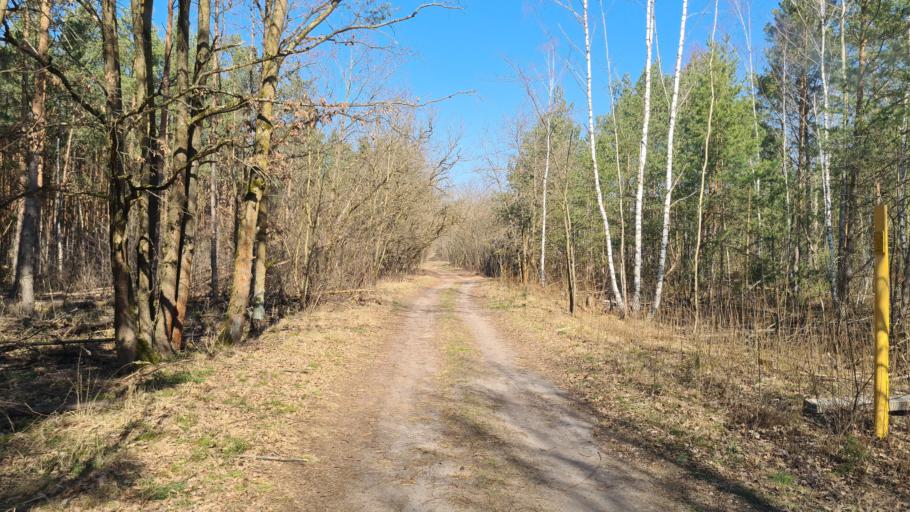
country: DE
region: Brandenburg
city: Finsterwalde
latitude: 51.5945
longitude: 13.7278
